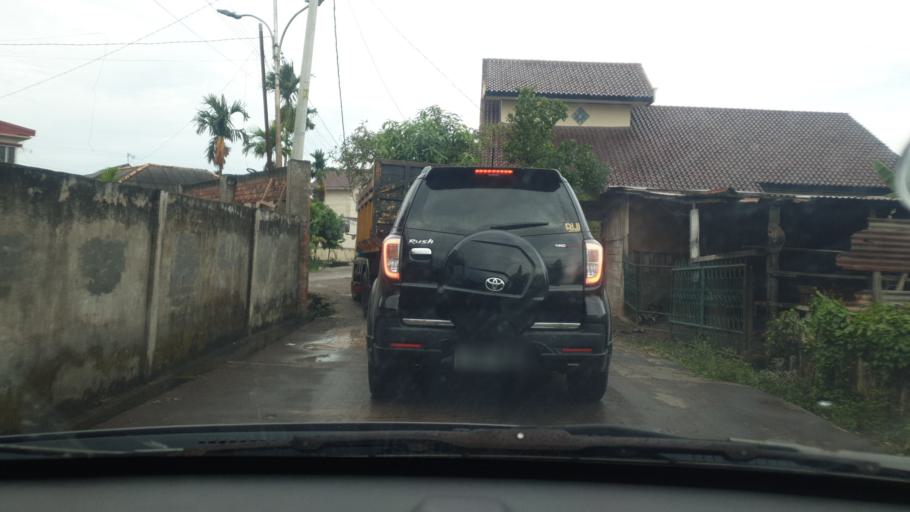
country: ID
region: South Sumatra
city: Palembang
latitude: -2.9736
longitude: 104.7181
